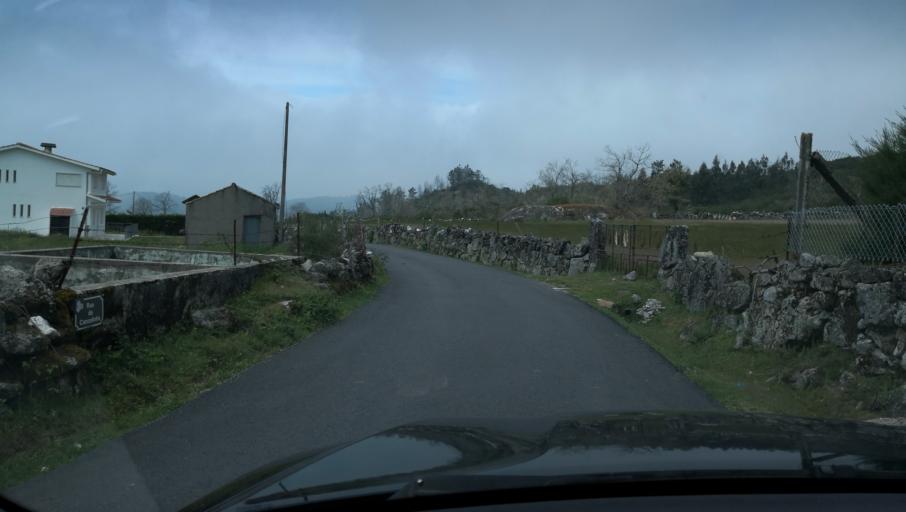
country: PT
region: Vila Real
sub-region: Vila Real
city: Vila Real
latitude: 41.2959
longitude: -7.8238
